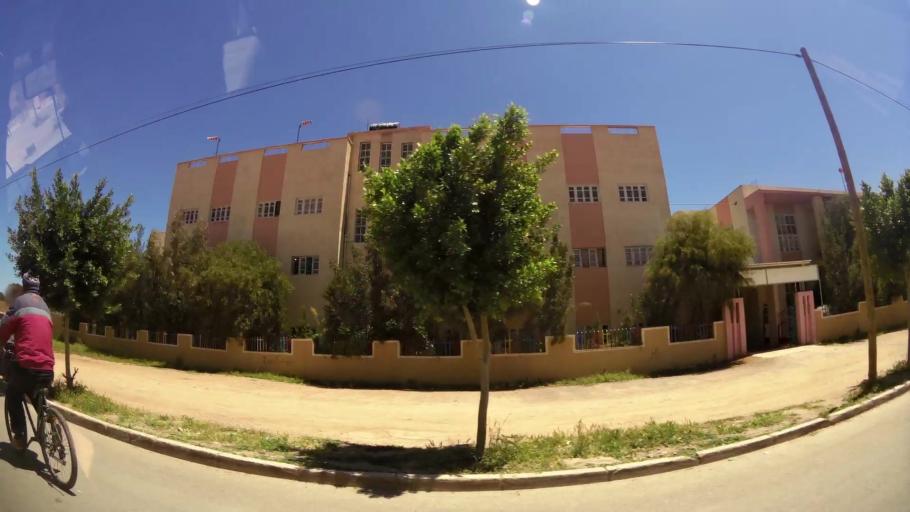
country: MA
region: Oriental
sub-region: Oujda-Angad
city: Oujda
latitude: 34.6683
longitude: -1.8823
